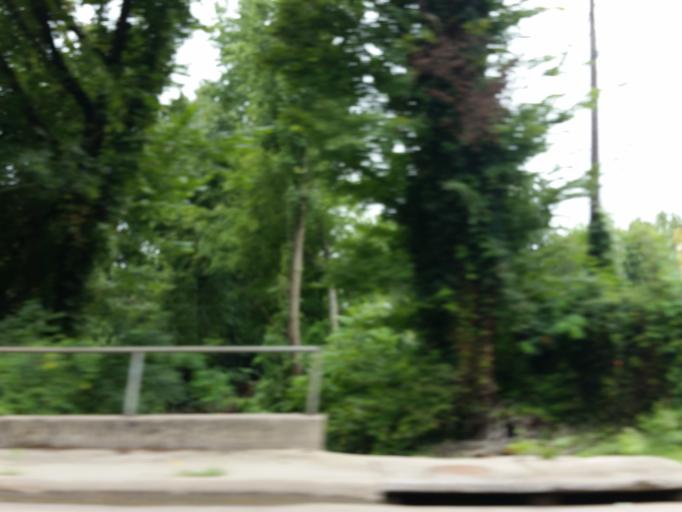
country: US
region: Missouri
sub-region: Cape Girardeau County
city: Cape Girardeau
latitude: 37.3333
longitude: -89.5469
